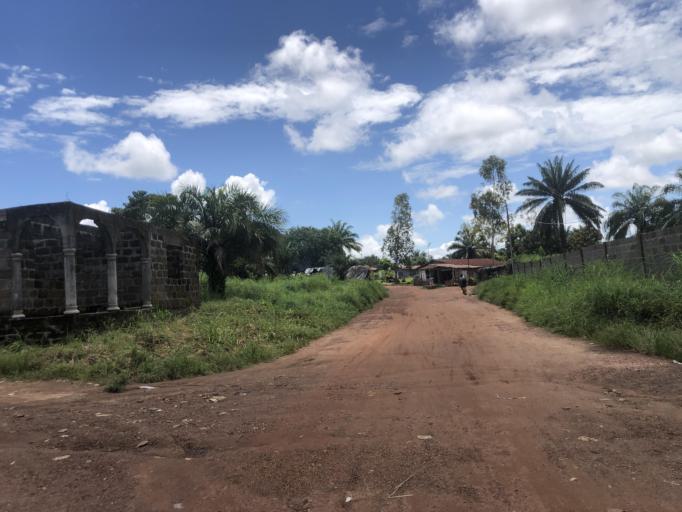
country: SL
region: Northern Province
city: Makeni
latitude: 8.8598
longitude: -12.0479
